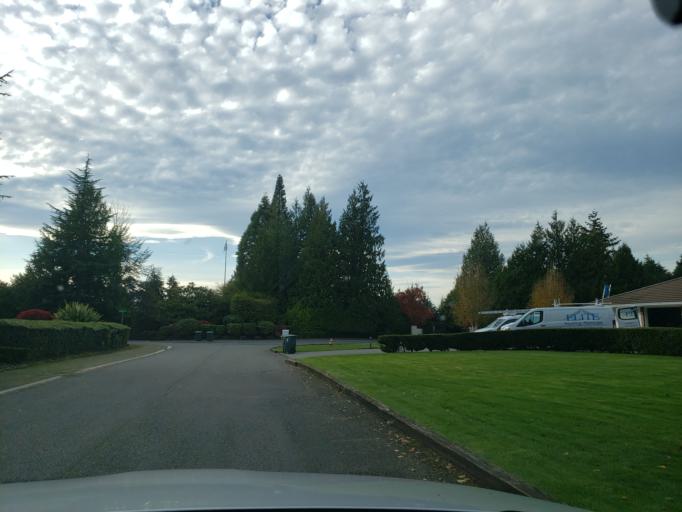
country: US
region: Washington
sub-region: Snohomish County
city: Woodway
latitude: 47.8002
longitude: -122.3896
